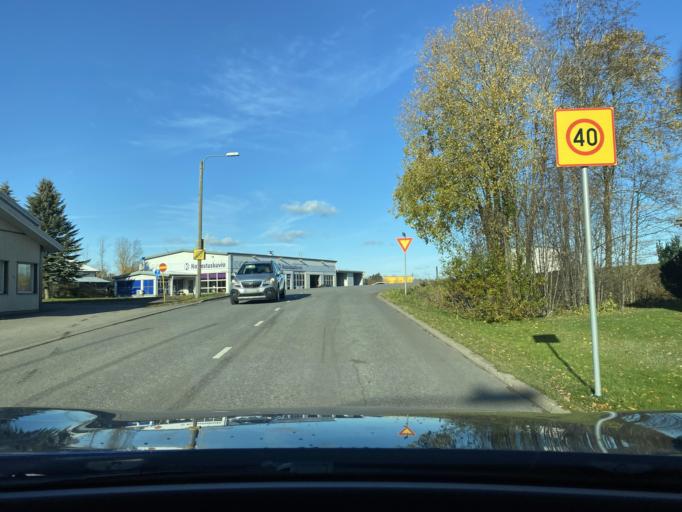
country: FI
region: Haeme
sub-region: Haemeenlinna
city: Haemeenlinna
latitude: 61.0144
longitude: 24.4101
